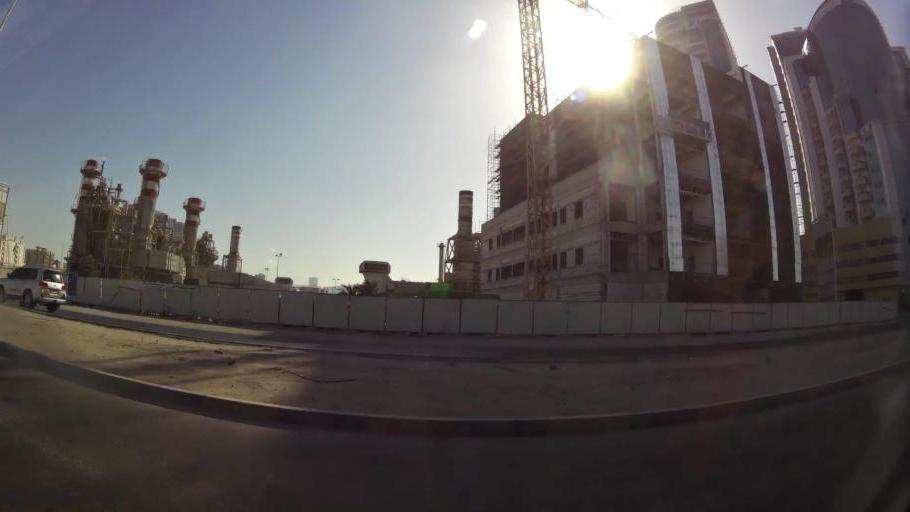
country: AE
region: Ajman
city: Ajman
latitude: 25.4036
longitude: 55.4522
